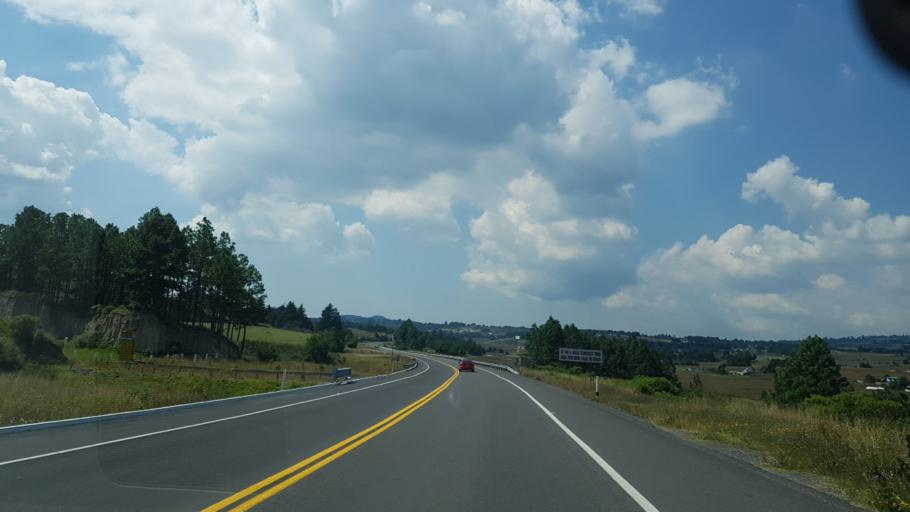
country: MX
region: Mexico
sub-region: Villa Victoria
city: Colonia Doctor Gustavo Baz
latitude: 19.3623
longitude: -99.9501
